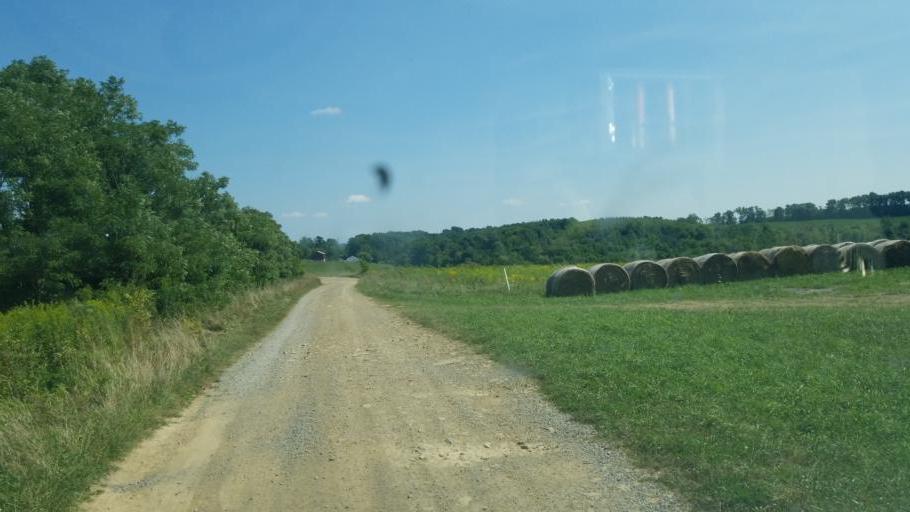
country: US
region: Pennsylvania
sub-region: Clarion County
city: Knox
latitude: 41.1040
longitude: -79.5308
